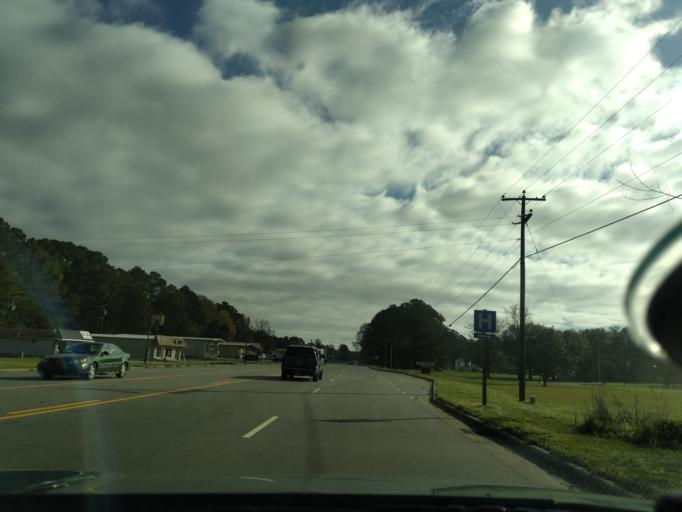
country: US
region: North Carolina
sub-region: Washington County
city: Plymouth
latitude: 35.8634
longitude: -76.7309
